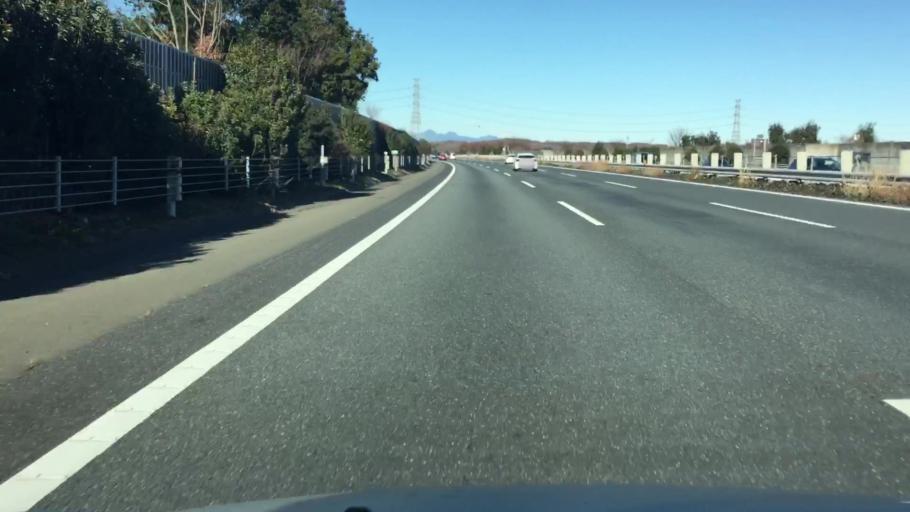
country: JP
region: Saitama
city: Honjo
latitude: 36.1973
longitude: 139.1854
